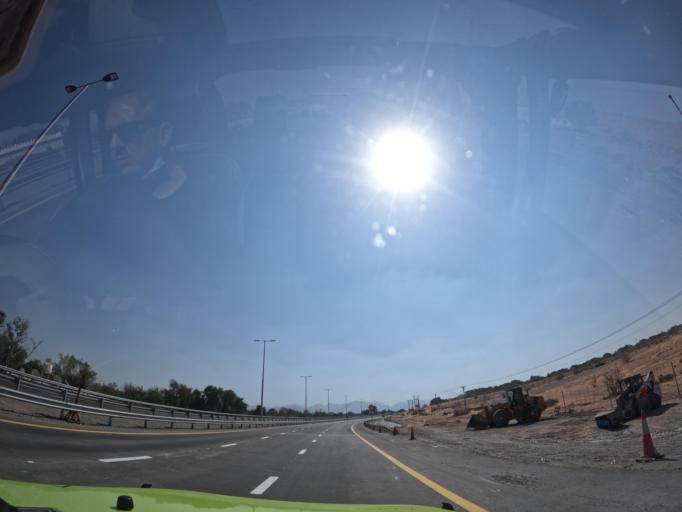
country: AE
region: Ash Shariqah
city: Adh Dhayd
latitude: 24.7905
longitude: 55.8127
